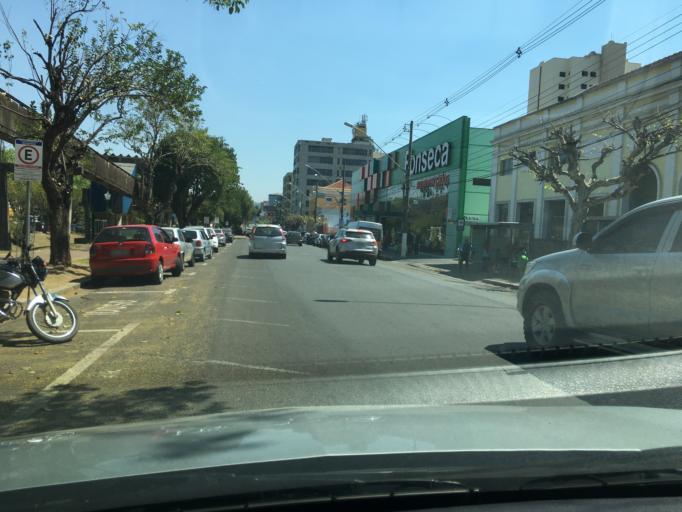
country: BR
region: Minas Gerais
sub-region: Pocos De Caldas
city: Pocos de Caldas
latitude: -21.7855
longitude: -46.5659
